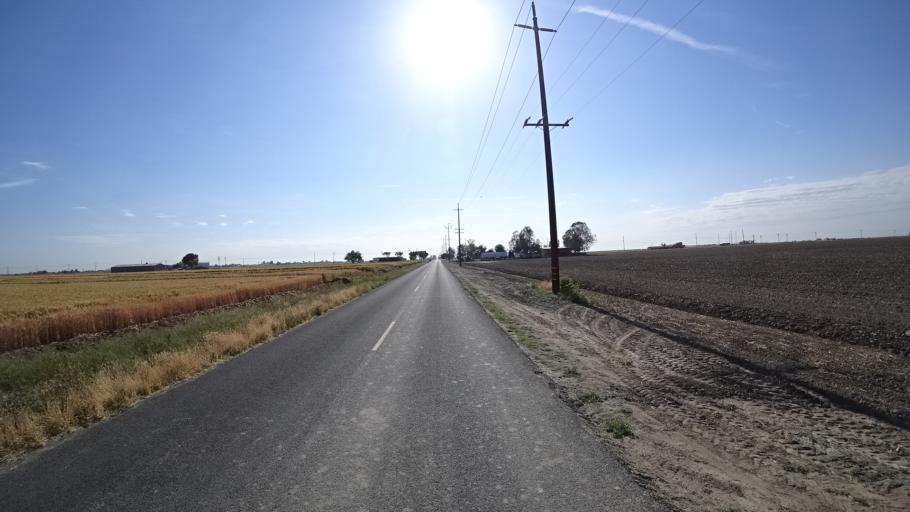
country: US
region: California
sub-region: Kings County
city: Stratford
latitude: 36.2258
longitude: -119.7842
